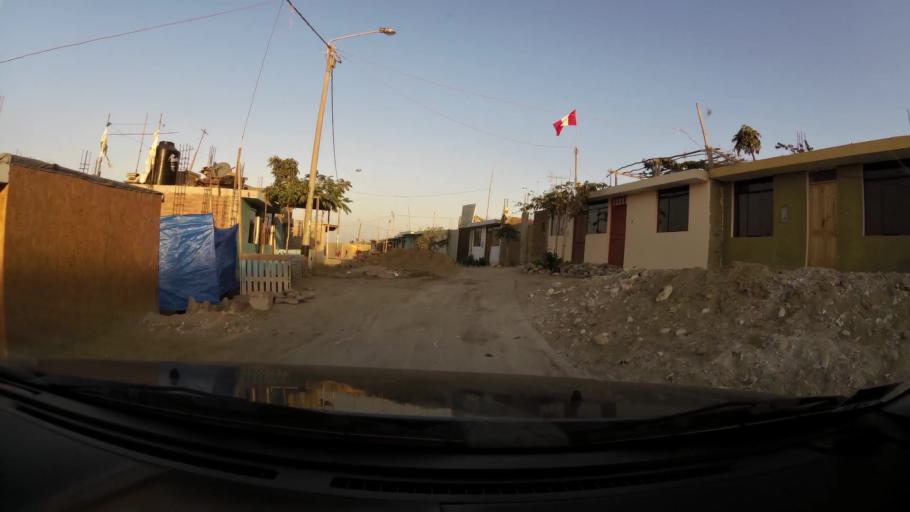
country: PE
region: Ica
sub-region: Provincia de Pisco
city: Villa Tupac Amaru
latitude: -13.6990
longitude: -76.1551
